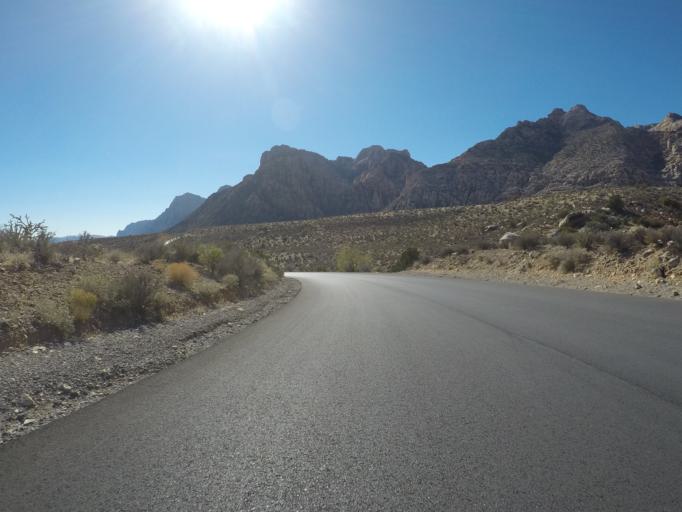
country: US
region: Nevada
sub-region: Clark County
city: Summerlin South
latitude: 36.1599
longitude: -115.4838
